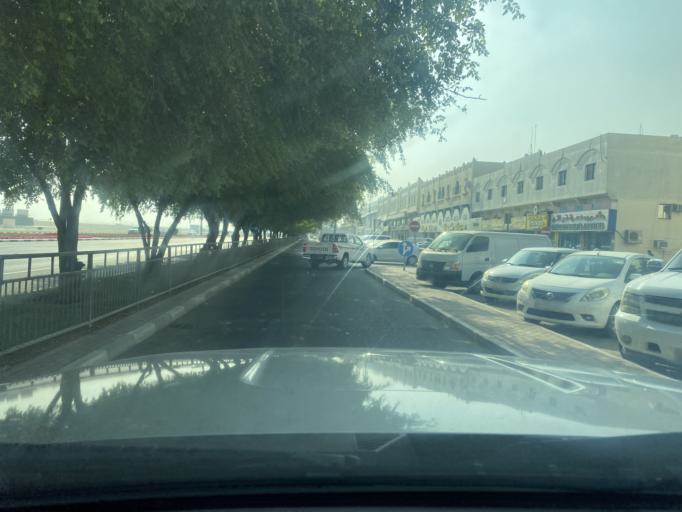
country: QA
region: Baladiyat ad Dawhah
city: Doha
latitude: 25.2414
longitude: 51.5703
